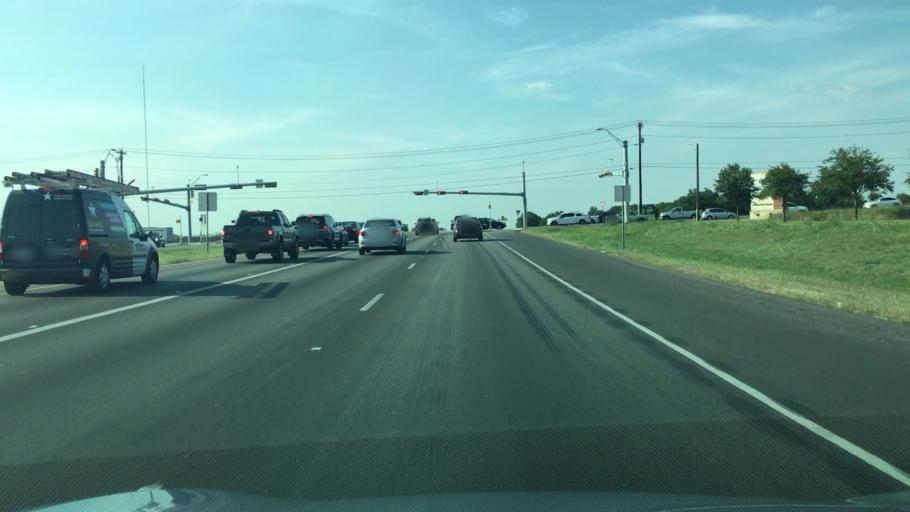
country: US
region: Texas
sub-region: Hays County
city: Kyle
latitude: 30.0272
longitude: -97.8724
